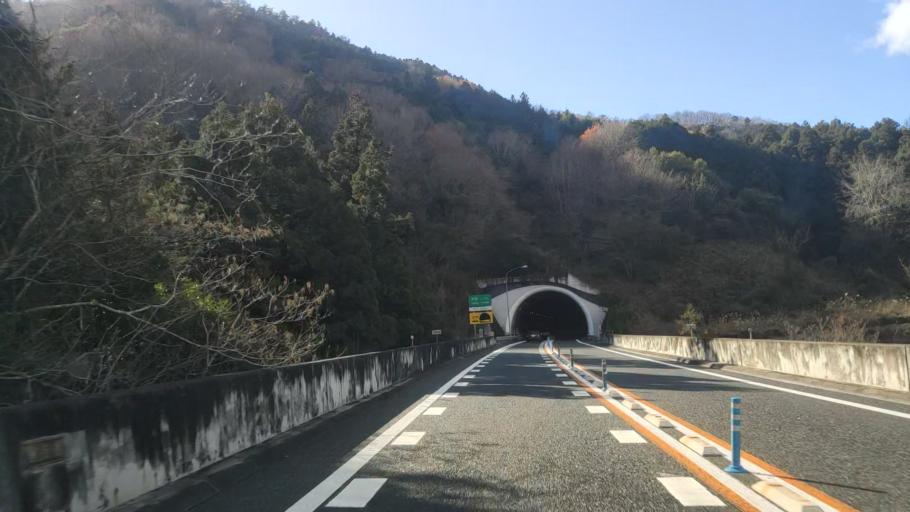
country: JP
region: Tokushima
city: Ikedacho
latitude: 34.0220
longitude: 133.8154
